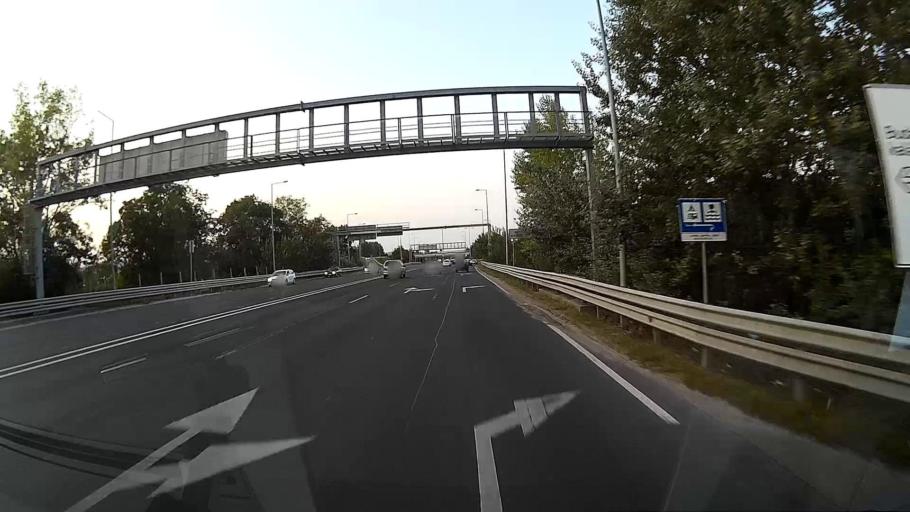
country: HU
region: Pest
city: Budakalasz
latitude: 47.6172
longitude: 19.0659
